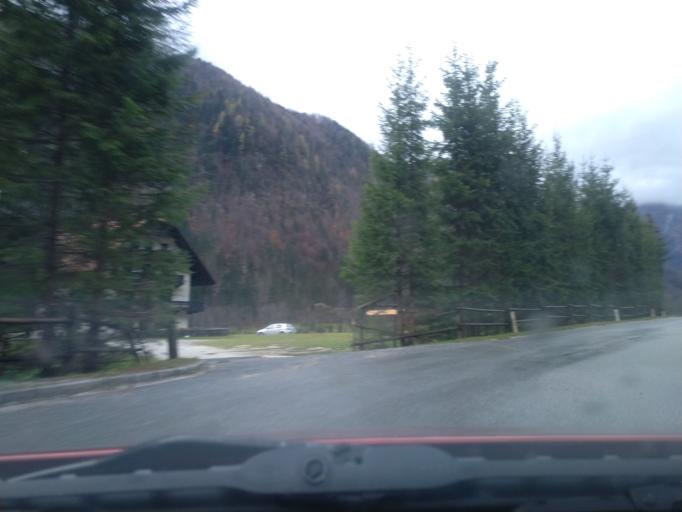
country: SI
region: Solcava
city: Solcava
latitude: 46.4188
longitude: 14.6416
